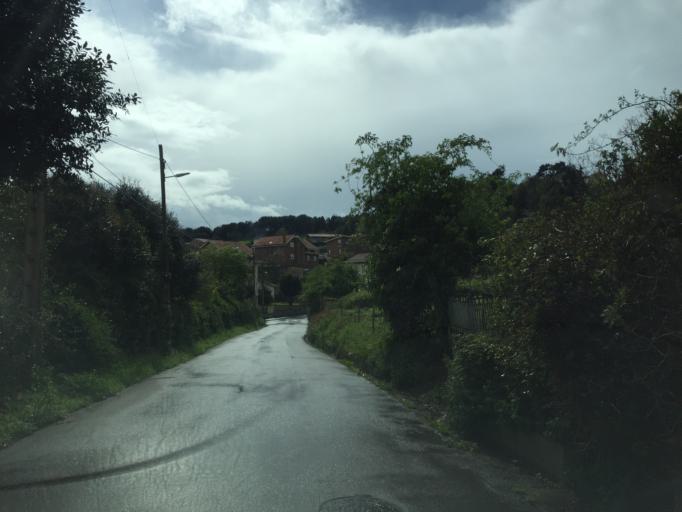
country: ES
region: Asturias
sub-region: Province of Asturias
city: Natahoyo
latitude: 43.5520
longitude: -5.7052
